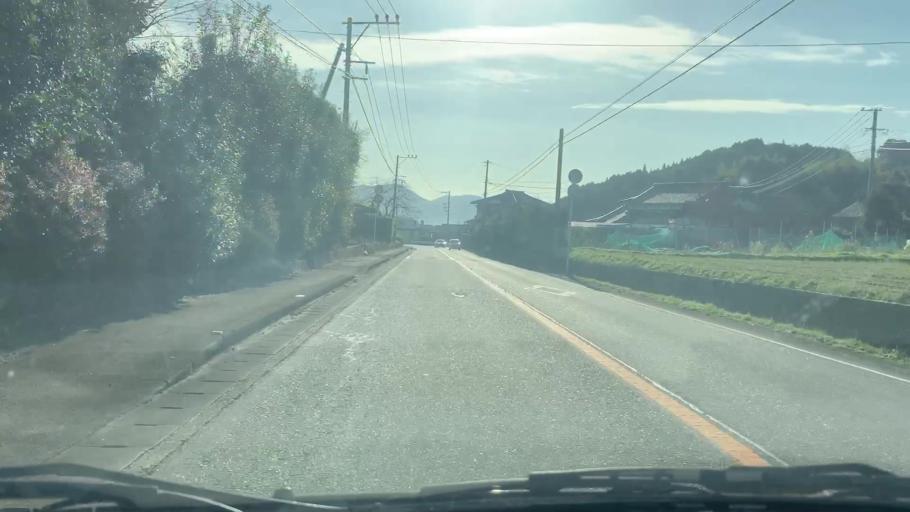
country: JP
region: Saga Prefecture
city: Takeocho-takeo
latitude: 33.2303
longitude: 130.0181
